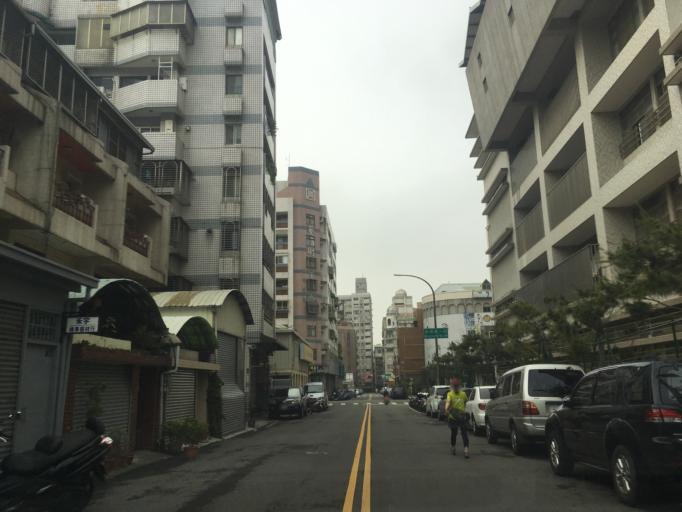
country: TW
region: Taiwan
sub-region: Taichung City
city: Taichung
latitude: 24.1760
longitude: 120.6777
